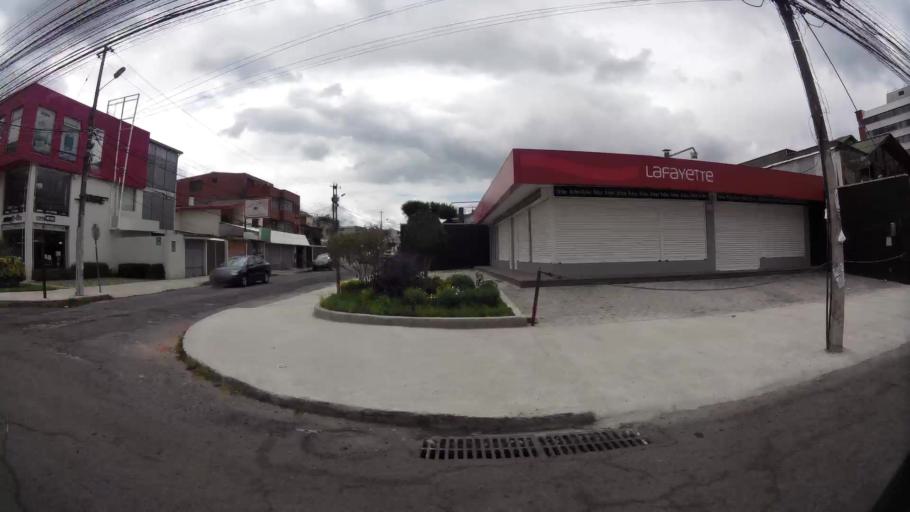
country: EC
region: Pichincha
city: Quito
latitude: -0.1677
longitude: -78.4808
